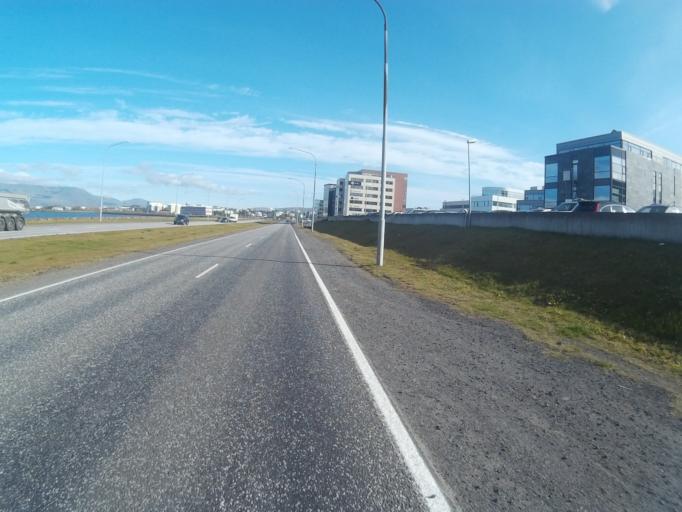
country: IS
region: Capital Region
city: Reykjavik
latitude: 64.1466
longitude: -21.9075
